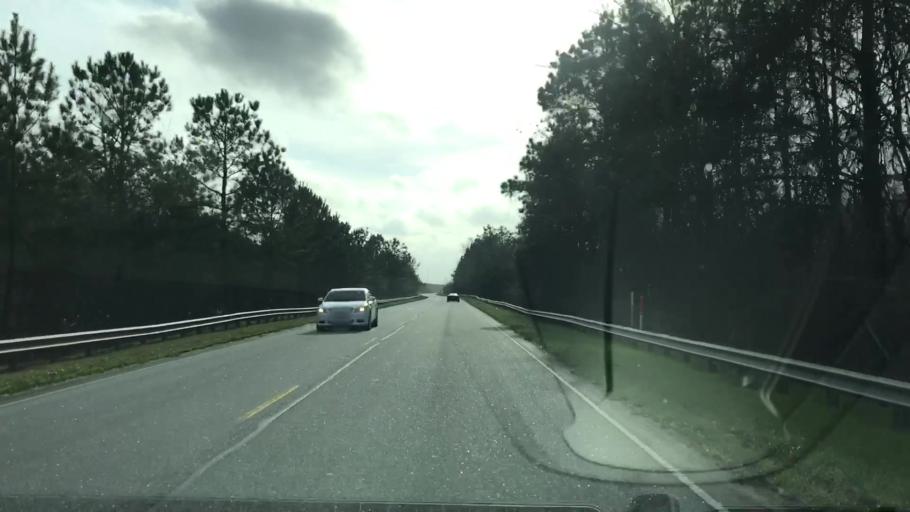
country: US
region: South Carolina
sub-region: Williamsburg County
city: Andrews
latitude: 33.3147
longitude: -79.6698
